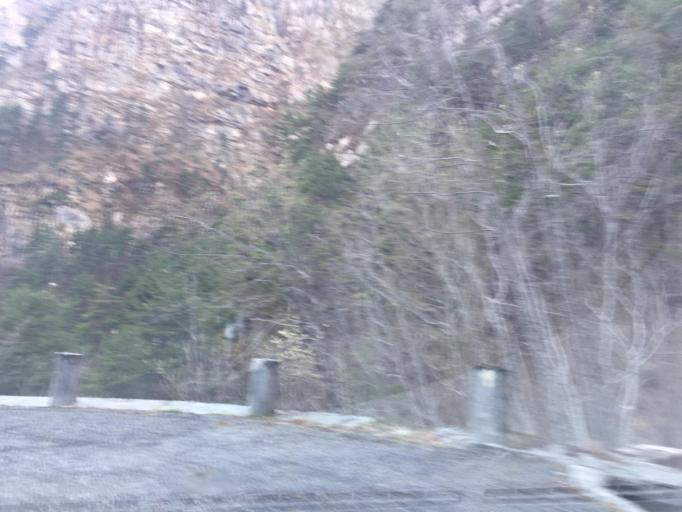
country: IT
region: Friuli Venezia Giulia
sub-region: Provincia di Udine
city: Amaro
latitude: 46.3869
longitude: 13.0794
